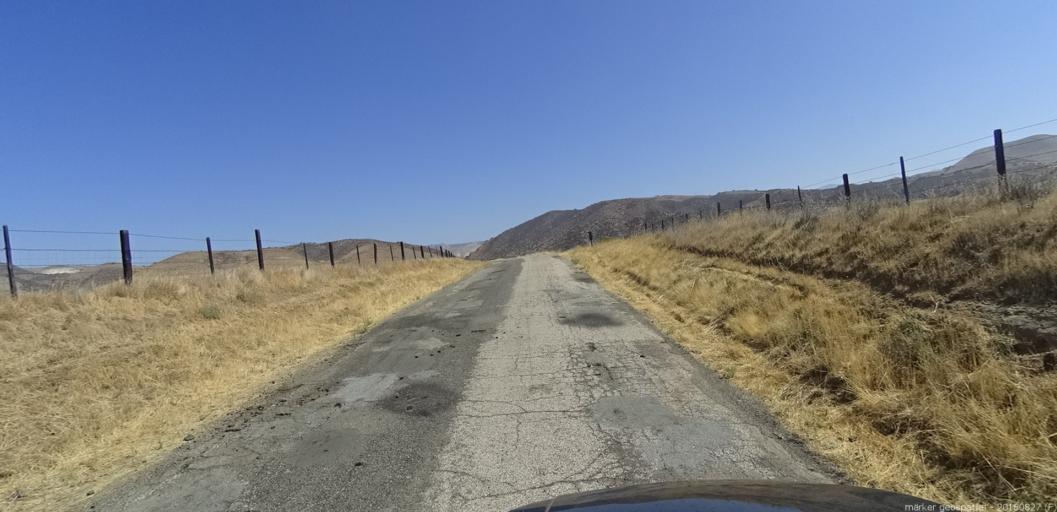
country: US
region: California
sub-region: Monterey County
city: King City
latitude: 36.2716
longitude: -120.9940
